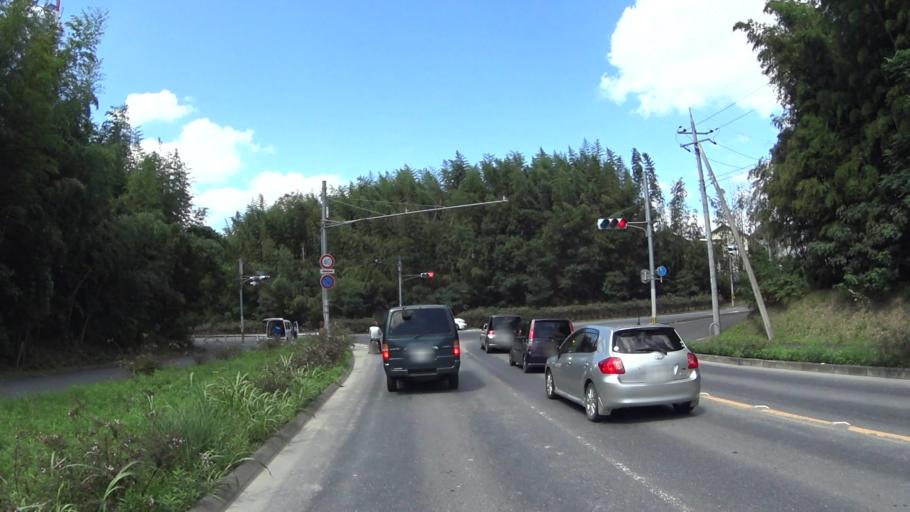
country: JP
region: Kyoto
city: Tanabe
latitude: 34.8479
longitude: 135.7891
